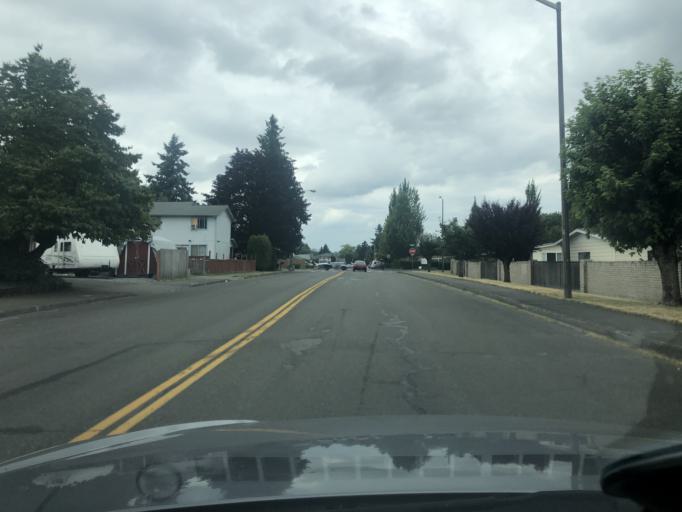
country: US
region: Washington
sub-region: King County
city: Auburn
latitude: 47.3257
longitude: -122.2141
